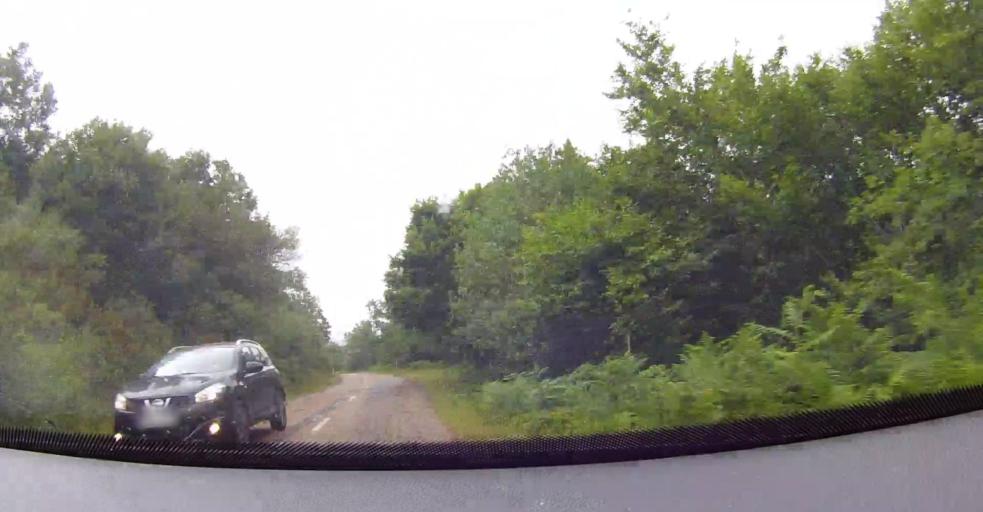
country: ES
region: Castille and Leon
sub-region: Provincia de Leon
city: Puebla de Lillo
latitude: 43.0620
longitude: -5.2722
